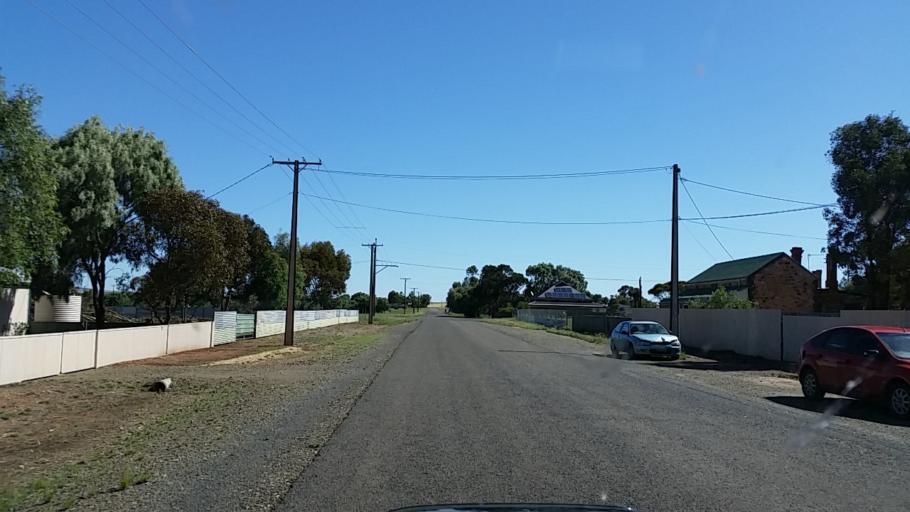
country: AU
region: South Australia
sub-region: Peterborough
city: Peterborough
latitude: -33.1513
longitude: 138.9173
